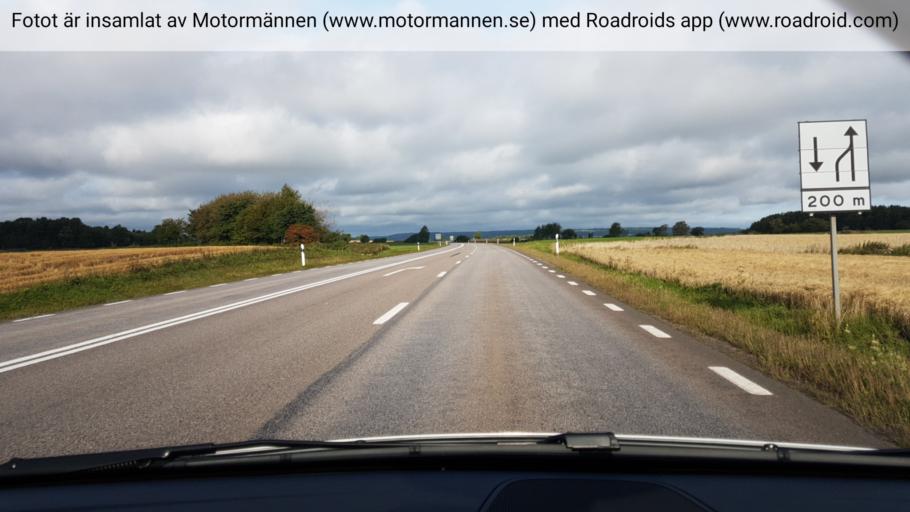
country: SE
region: Vaestra Goetaland
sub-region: Falkopings Kommun
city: Falkoeping
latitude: 58.1451
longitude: 13.6218
